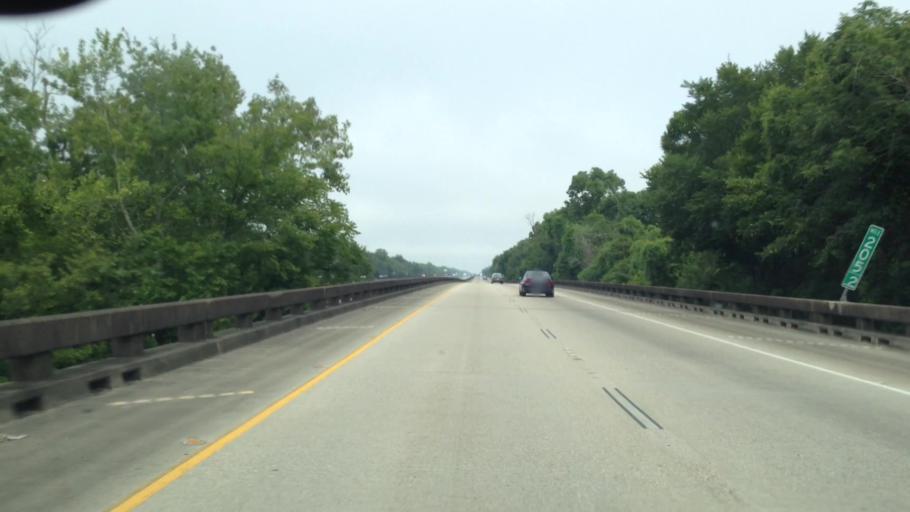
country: US
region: Louisiana
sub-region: Saint John the Baptist Parish
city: Montegut
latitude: 30.1080
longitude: -90.5084
